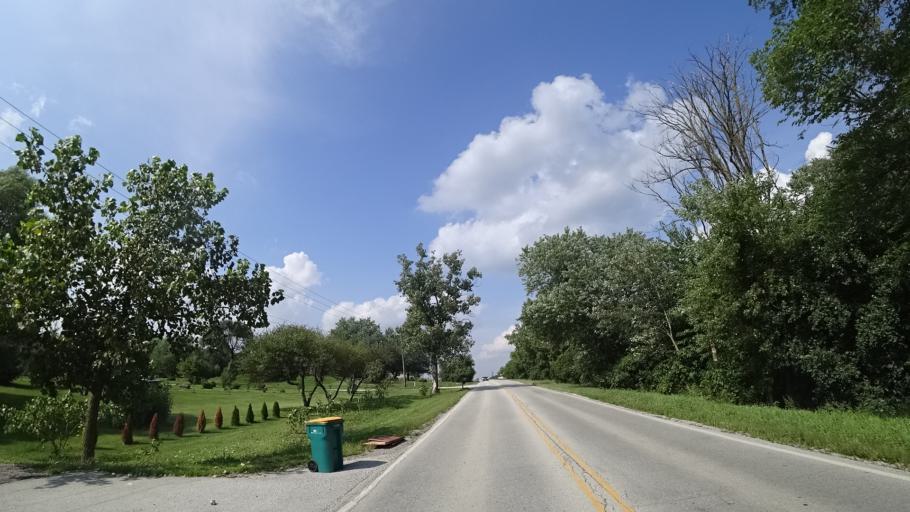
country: US
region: Illinois
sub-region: Will County
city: Goodings Grove
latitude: 41.6459
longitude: -87.9315
